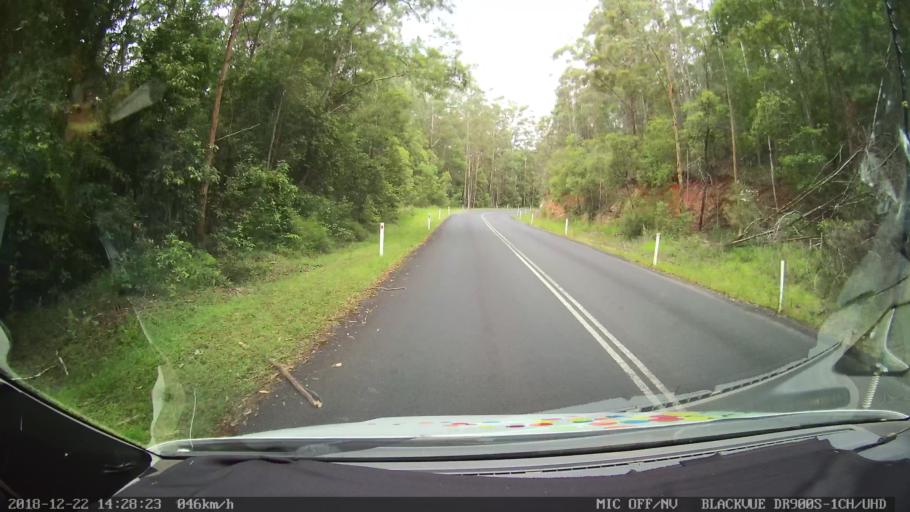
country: AU
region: New South Wales
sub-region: Bellingen
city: Dorrigo
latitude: -30.0727
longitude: 152.6358
